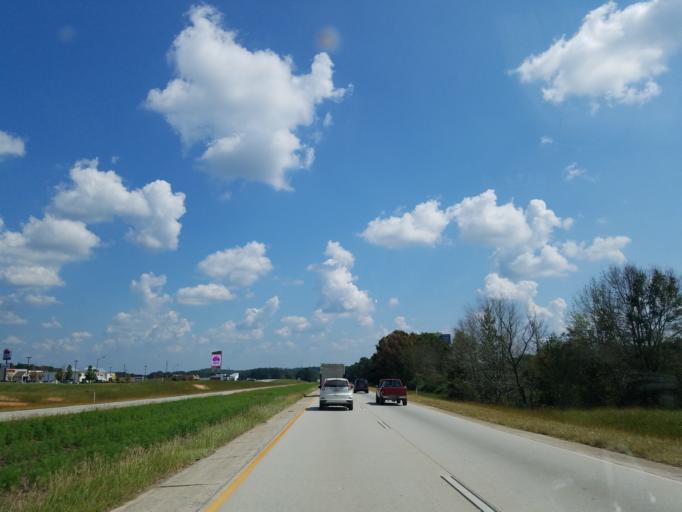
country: US
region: Georgia
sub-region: Barrow County
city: Winder
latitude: 33.9423
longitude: -83.7449
